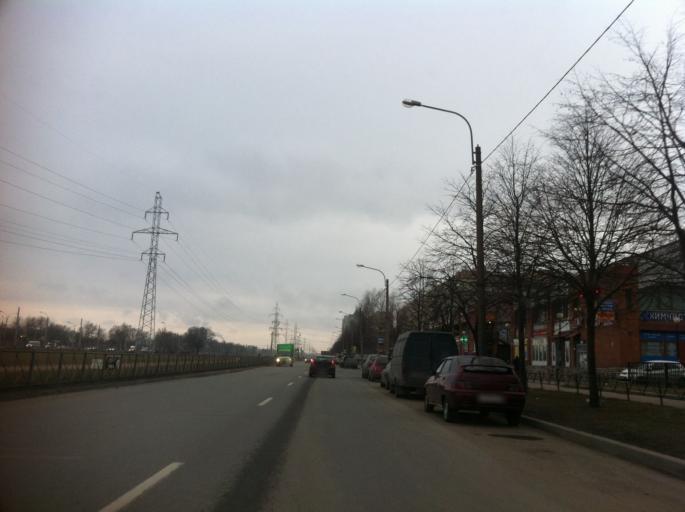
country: RU
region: St.-Petersburg
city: Uritsk
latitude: 59.8466
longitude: 30.2079
